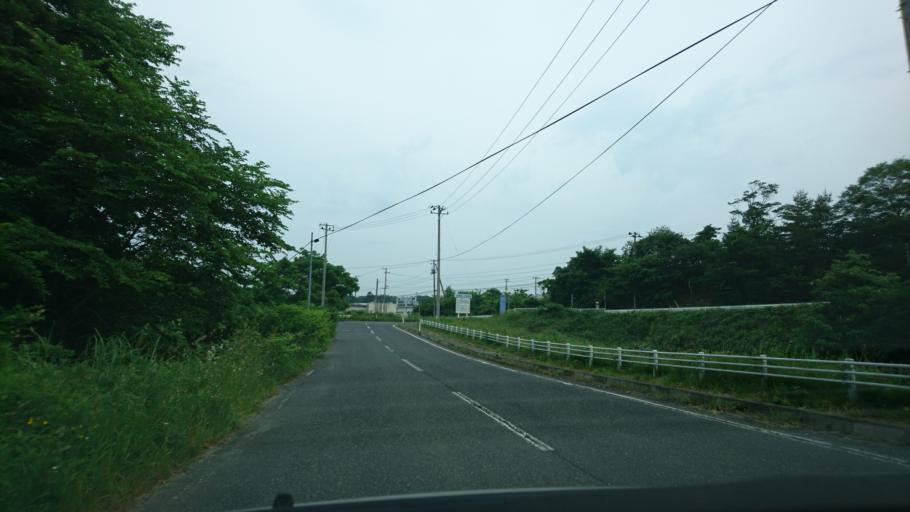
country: JP
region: Iwate
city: Ichinoseki
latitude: 38.8844
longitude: 141.1362
